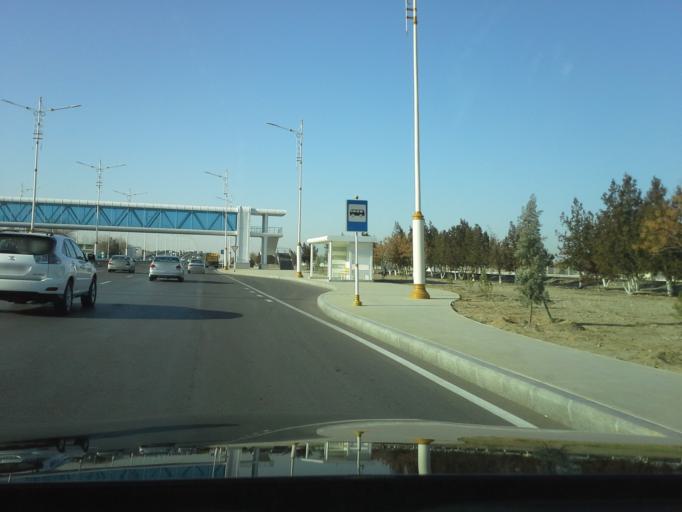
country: TM
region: Ahal
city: Ashgabat
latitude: 37.9589
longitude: 58.3671
